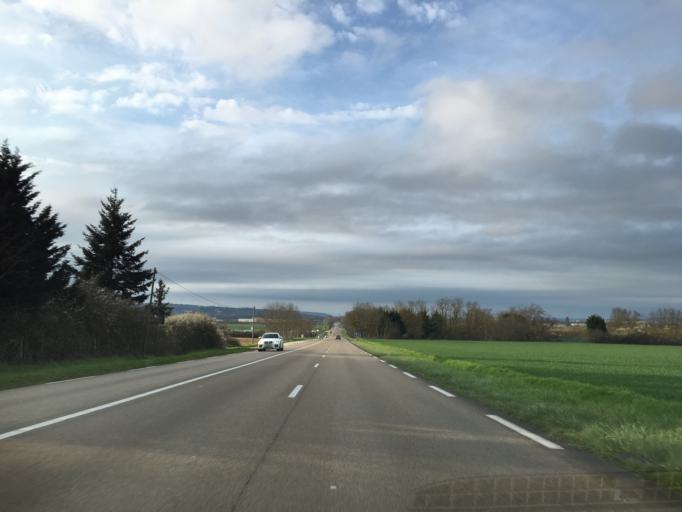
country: FR
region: Bourgogne
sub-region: Departement de l'Yonne
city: Maillot
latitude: 48.1583
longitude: 3.3044
